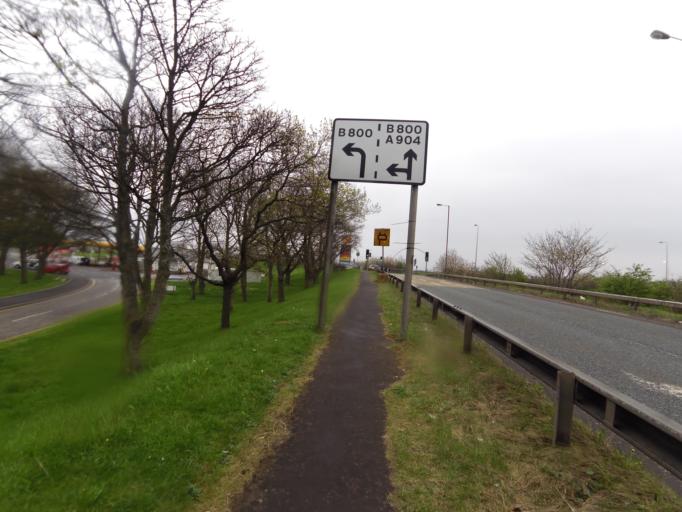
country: GB
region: Scotland
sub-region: Edinburgh
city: Queensferry
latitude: 55.9851
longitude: -3.4037
